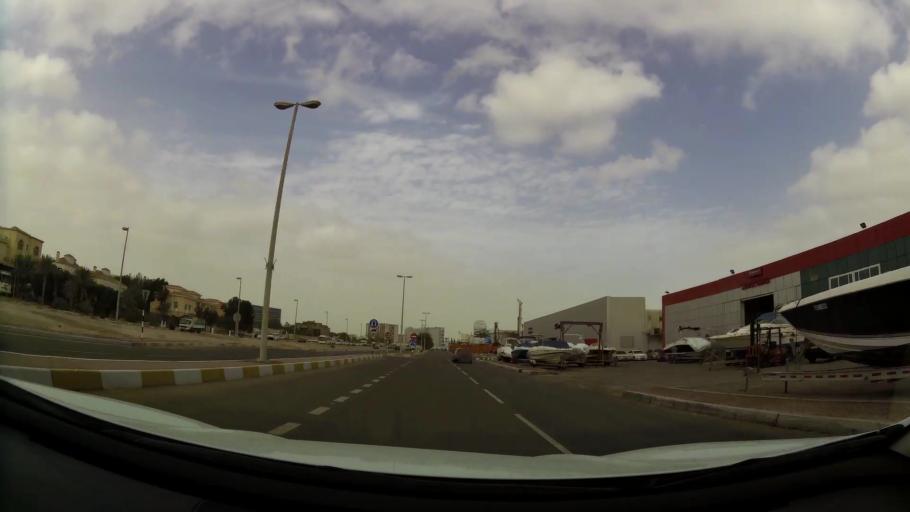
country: AE
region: Abu Dhabi
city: Abu Dhabi
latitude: 24.4150
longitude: 54.4972
